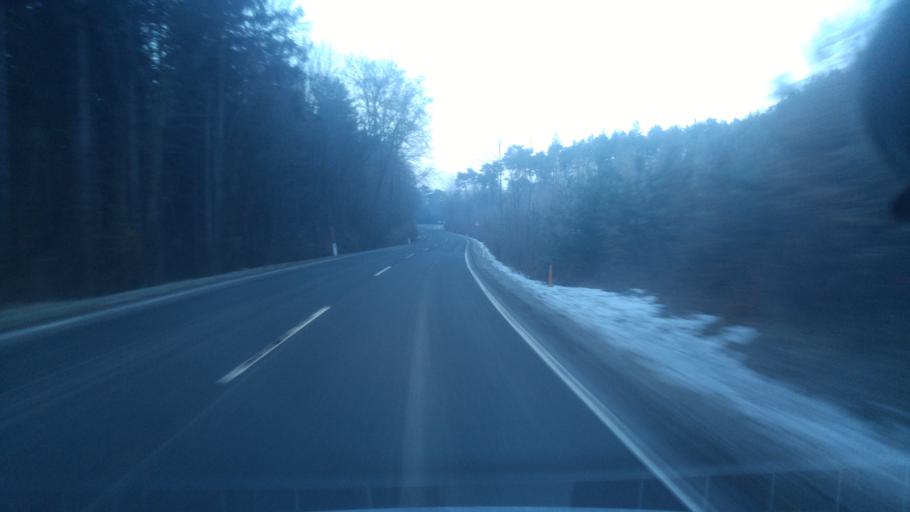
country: AT
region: Lower Austria
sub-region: Politischer Bezirk Baden
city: Berndorf
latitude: 47.9531
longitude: 16.1308
